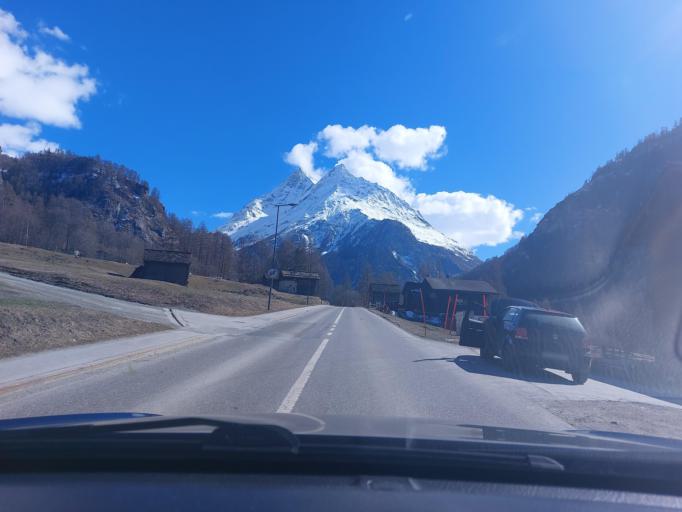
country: CH
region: Valais
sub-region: Herens District
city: Evolene
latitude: 46.1051
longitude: 7.5025
